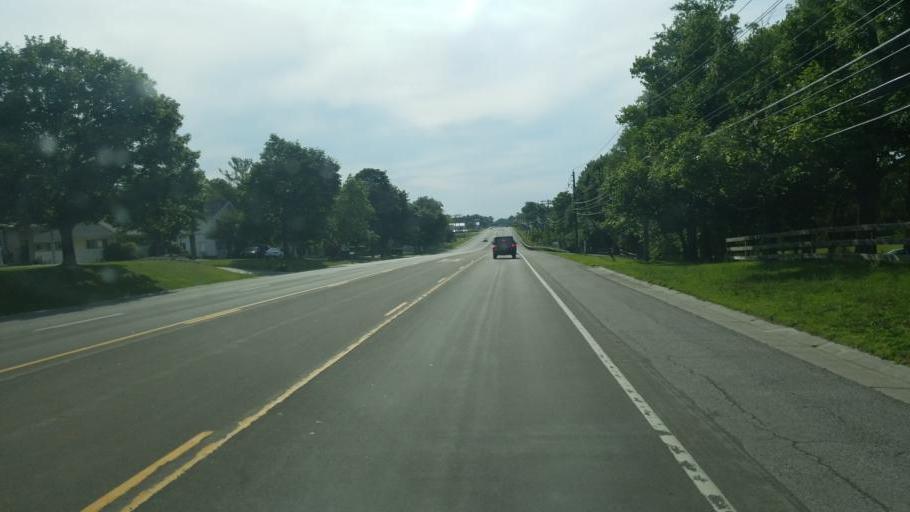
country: US
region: New York
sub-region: Genesee County
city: Batavia
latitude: 42.9900
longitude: -78.1354
